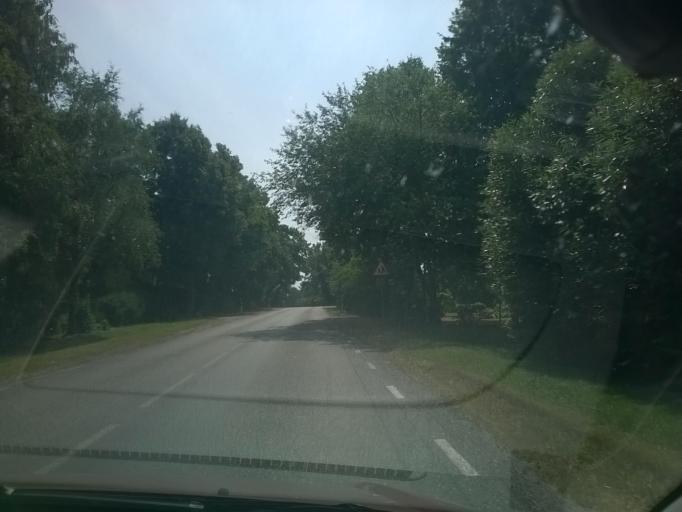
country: EE
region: Tartu
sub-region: Puhja vald
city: Puhja
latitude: 58.2831
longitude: 26.1752
